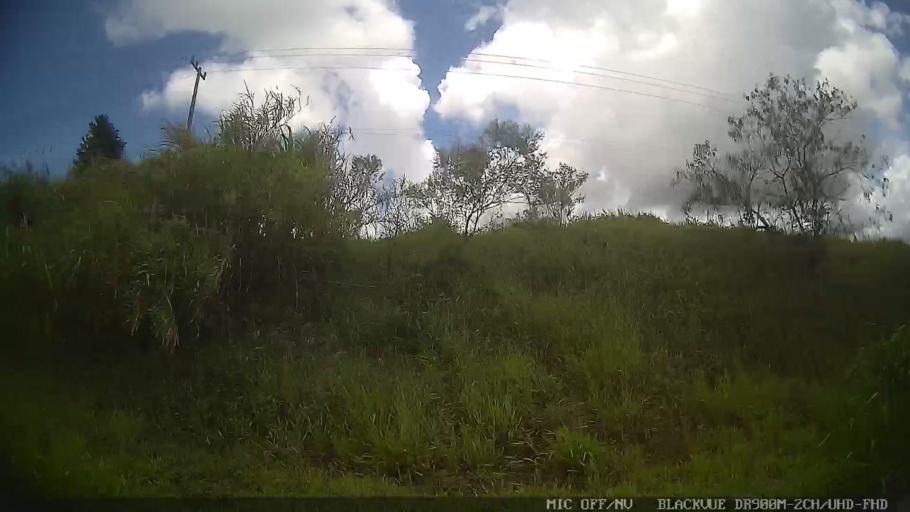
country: BR
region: Sao Paulo
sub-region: Braganca Paulista
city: Braganca Paulista
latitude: -22.8460
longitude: -46.6428
